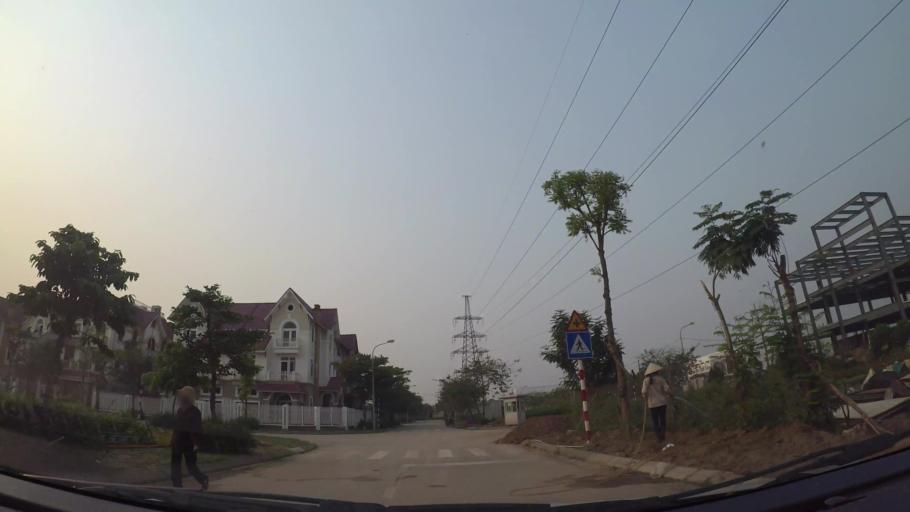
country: VN
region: Ha Noi
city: Cau Dien
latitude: 21.0071
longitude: 105.7343
